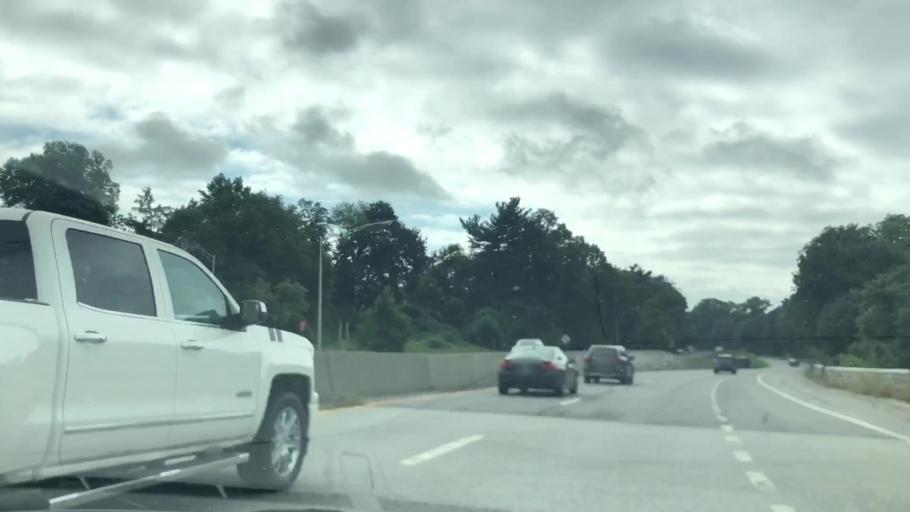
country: US
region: New York
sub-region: Westchester County
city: Yonkers
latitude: 40.9554
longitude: -73.8715
